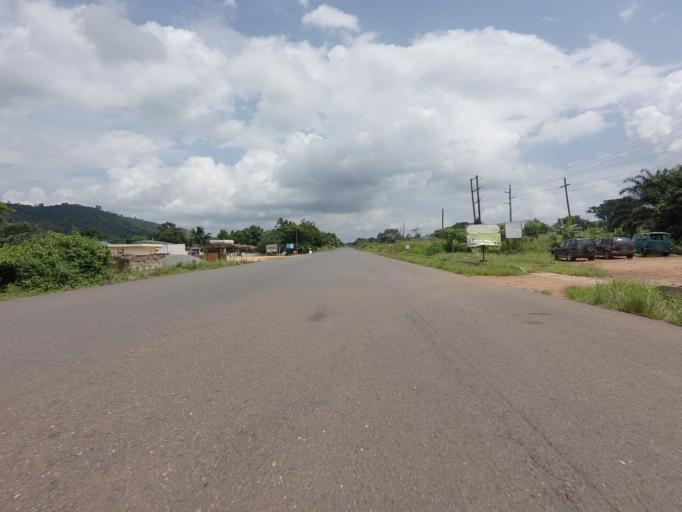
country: GH
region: Volta
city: Ho
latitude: 6.5087
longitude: 0.2129
